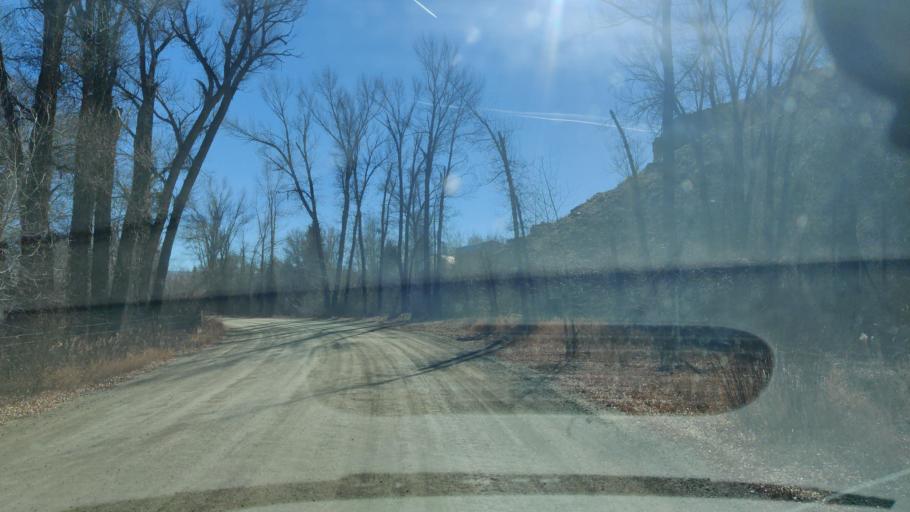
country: US
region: Colorado
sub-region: Gunnison County
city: Gunnison
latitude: 38.5383
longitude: -106.9510
